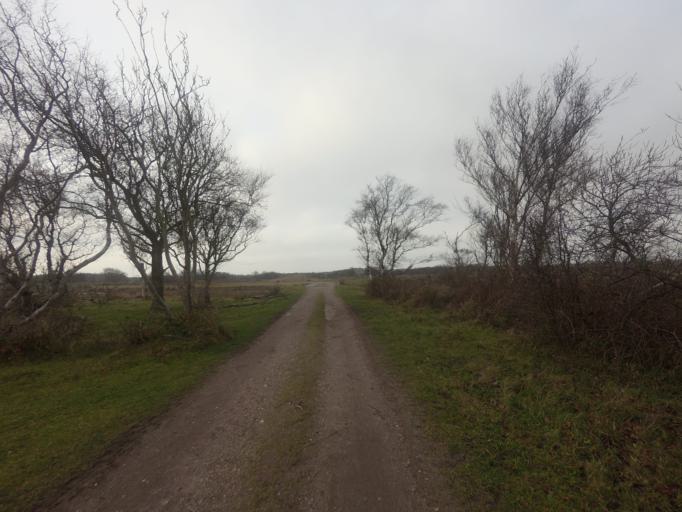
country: NL
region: North Holland
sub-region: Gemeente Texel
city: Den Burg
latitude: 53.1208
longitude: 4.8004
